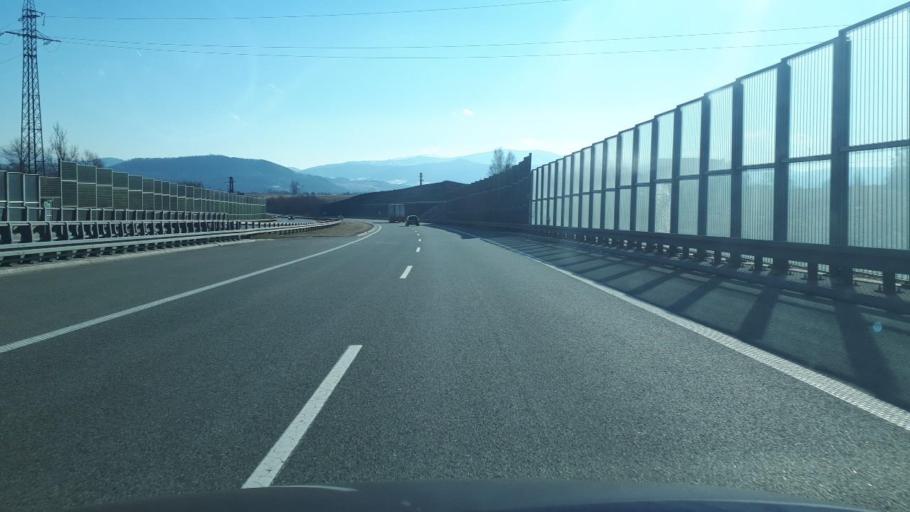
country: PL
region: Silesian Voivodeship
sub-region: Powiat zywiecki
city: Lesna
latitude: 49.6889
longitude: 19.1382
